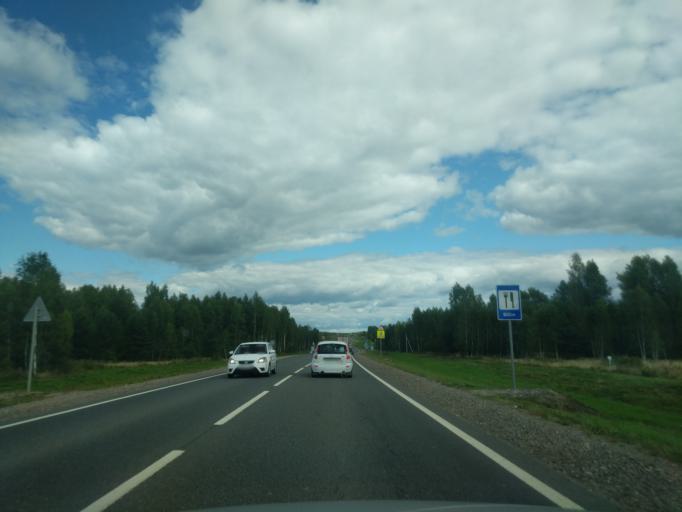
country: RU
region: Kostroma
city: Oktyabr'skiy
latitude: 57.8042
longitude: 41.2892
